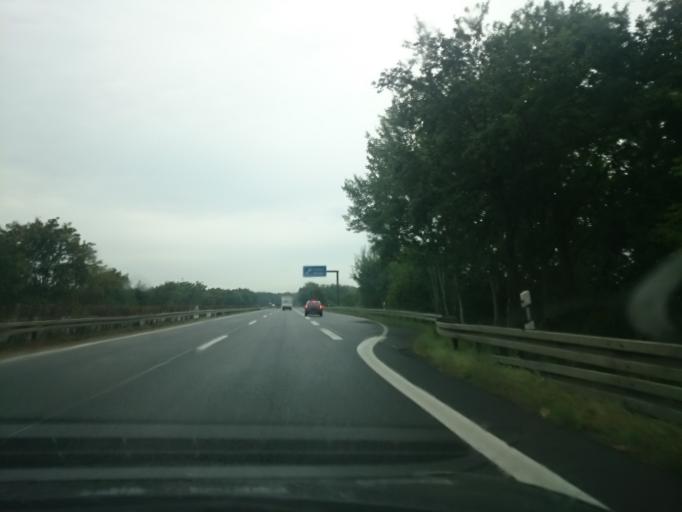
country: DE
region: Brandenburg
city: Werder
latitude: 52.4125
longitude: 12.9015
